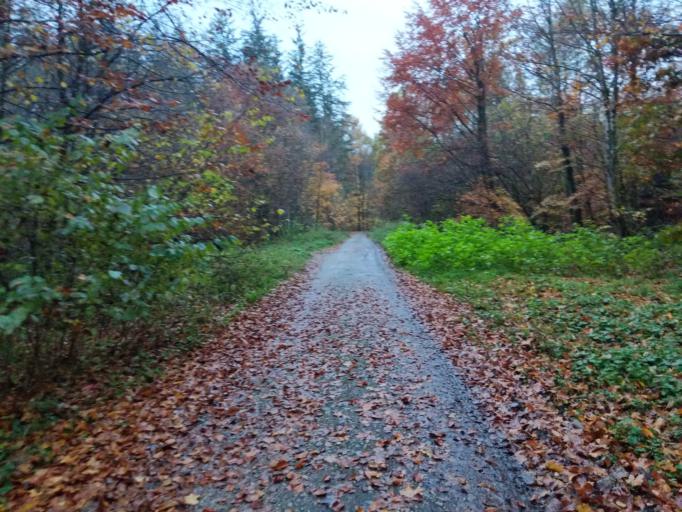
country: DE
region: Bavaria
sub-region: Upper Bavaria
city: Zorneding
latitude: 48.0898
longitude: 11.8482
